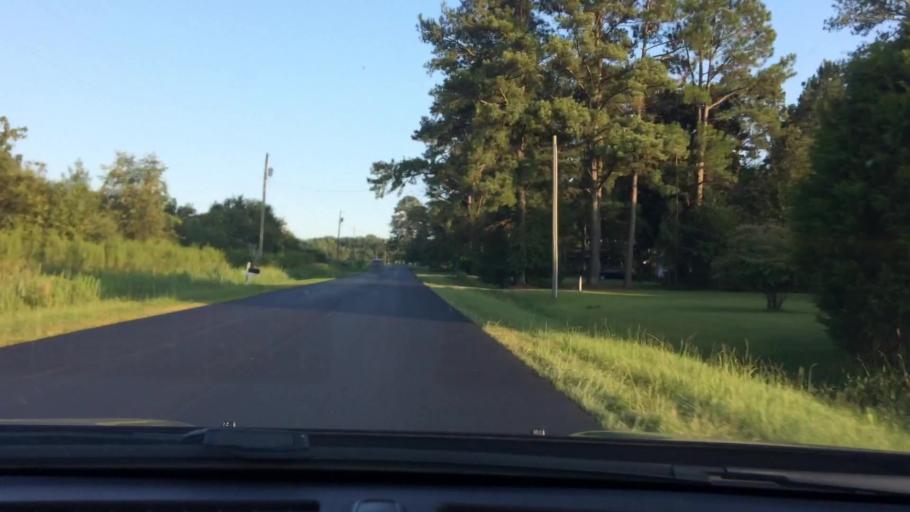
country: US
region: North Carolina
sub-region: Pitt County
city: Ayden
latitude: 35.4502
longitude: -77.4646
